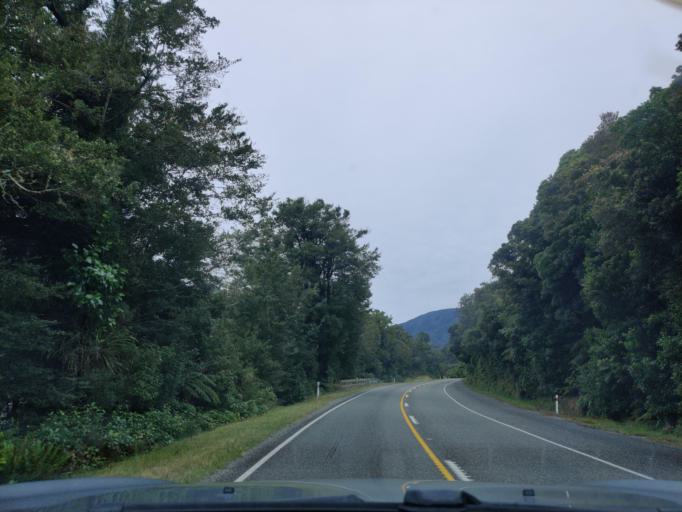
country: NZ
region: West Coast
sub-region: Buller District
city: Westport
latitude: -41.8300
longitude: 171.6472
